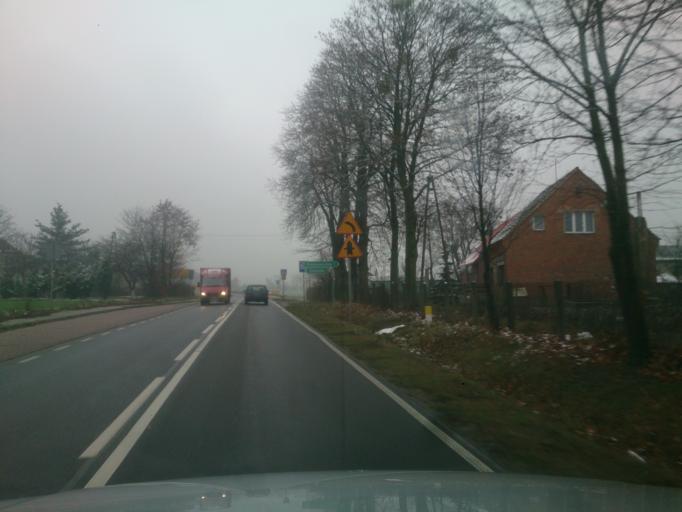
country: PL
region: Kujawsko-Pomorskie
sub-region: Powiat brodnicki
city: Brodnica
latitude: 53.2041
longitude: 19.3839
